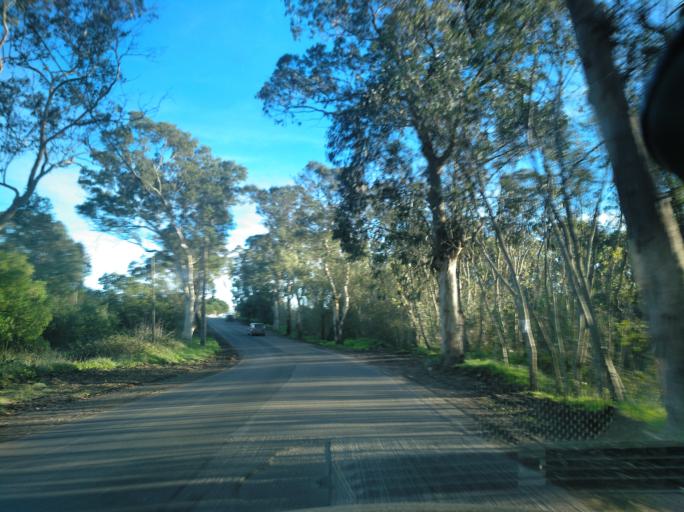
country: PT
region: Lisbon
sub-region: Sintra
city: Sintra
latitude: 38.8210
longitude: -9.3680
